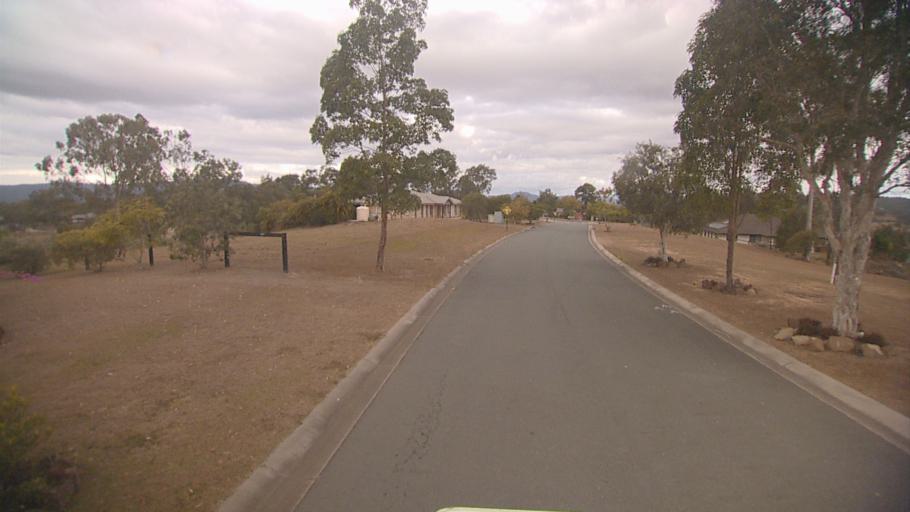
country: AU
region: Queensland
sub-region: Logan
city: Cedar Vale
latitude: -27.8729
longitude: 153.0741
